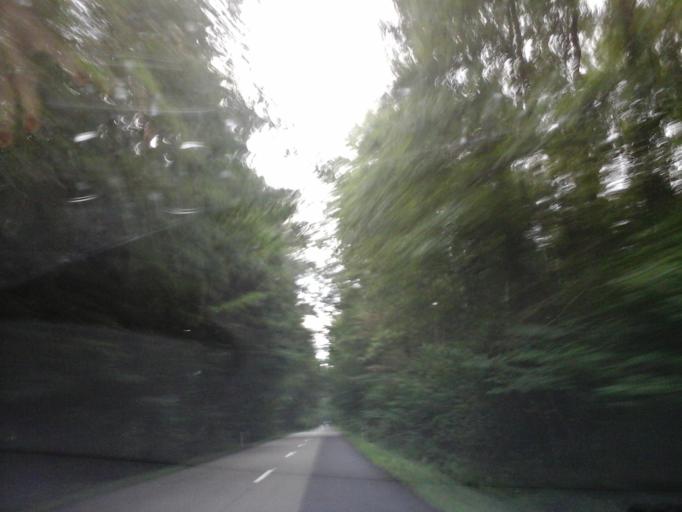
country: PL
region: West Pomeranian Voivodeship
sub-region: Powiat kamienski
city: Golczewo
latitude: 53.7809
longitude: 15.0216
